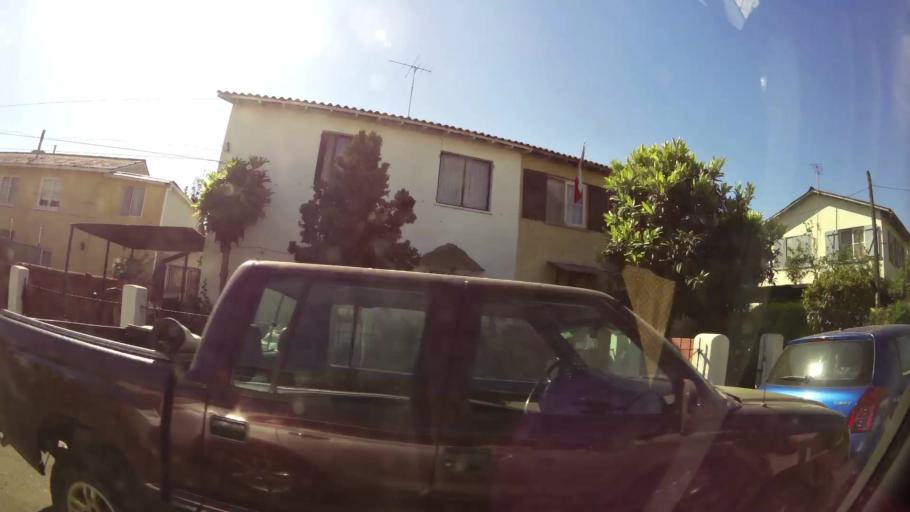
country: CL
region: Santiago Metropolitan
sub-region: Provincia de Talagante
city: Penaflor
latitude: -33.6043
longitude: -70.8999
